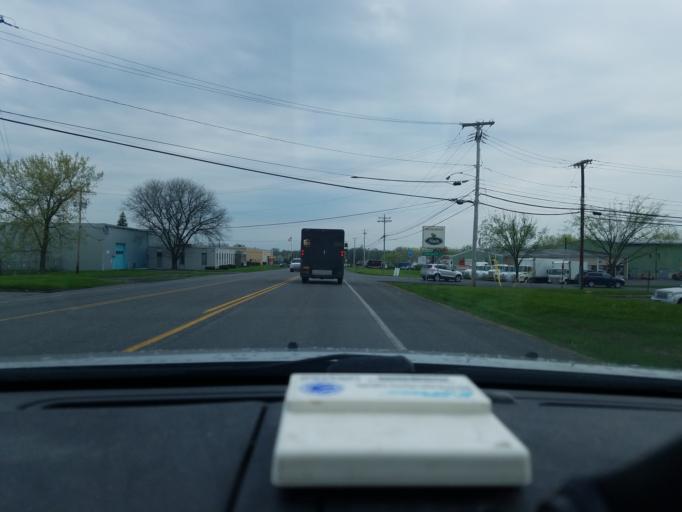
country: US
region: New York
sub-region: Onondaga County
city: East Syracuse
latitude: 43.0998
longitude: -76.0869
